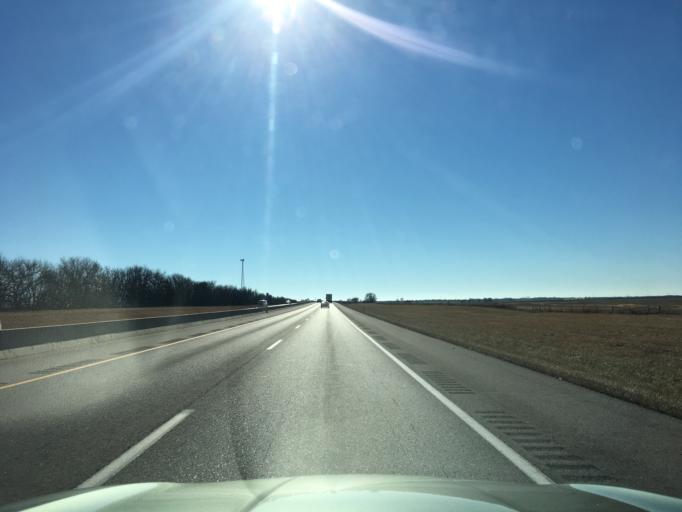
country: US
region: Kansas
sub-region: Sumner County
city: Wellington
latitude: 37.1241
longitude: -97.3389
